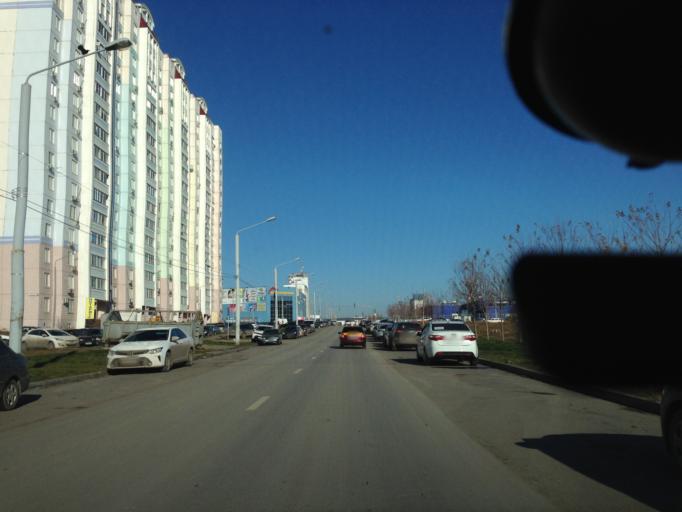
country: RU
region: Rostov
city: Kalinin
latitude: 47.2333
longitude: 39.6053
